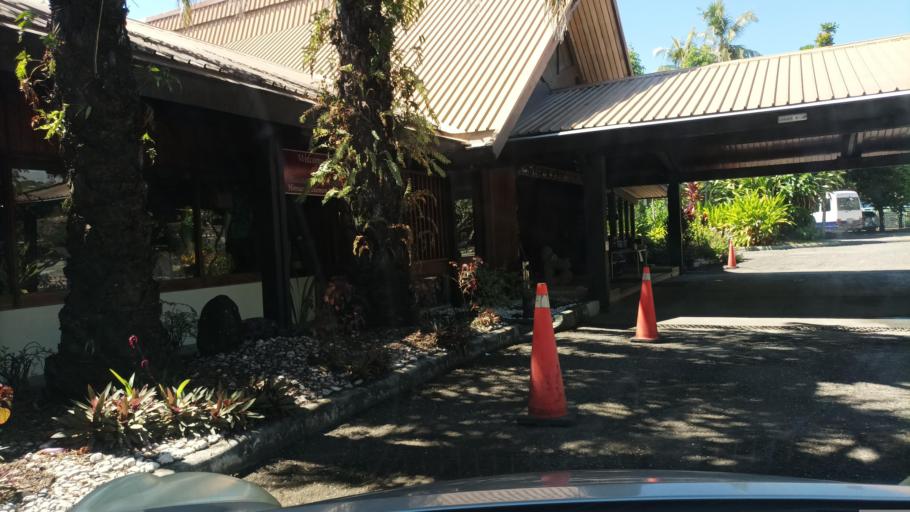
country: SB
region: Guadalcanal
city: Honiara
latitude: -9.4302
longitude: 159.9540
